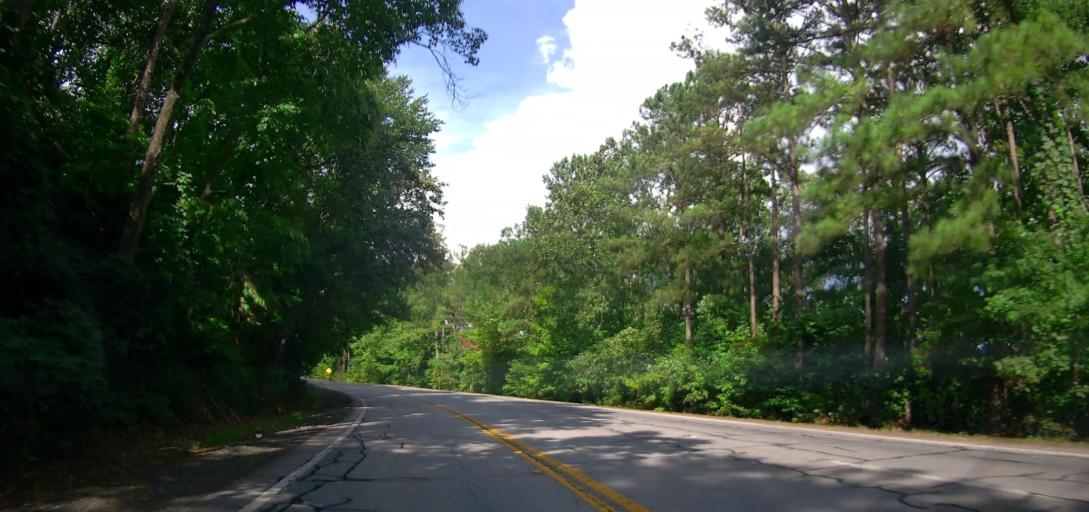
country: US
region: Georgia
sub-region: Harris County
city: Hamilton
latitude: 32.8058
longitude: -84.8606
